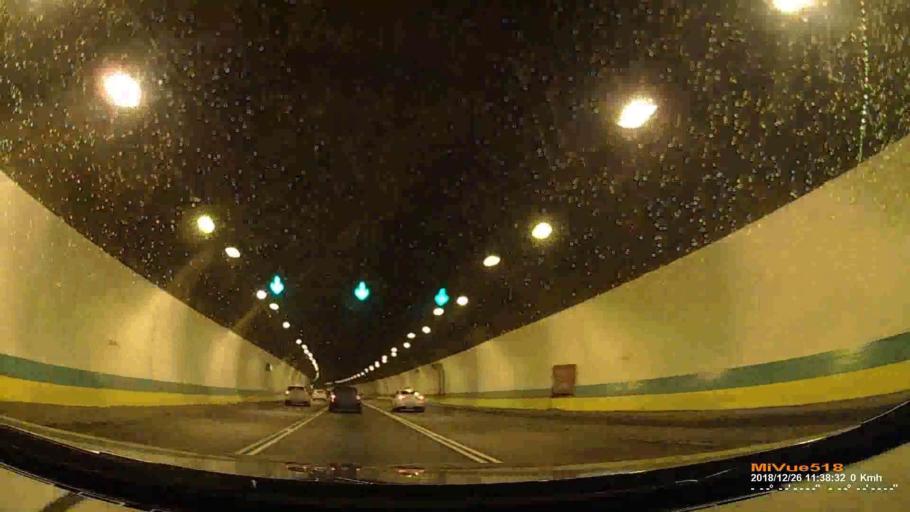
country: TW
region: Taipei
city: Taipei
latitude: 24.9813
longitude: 121.5853
